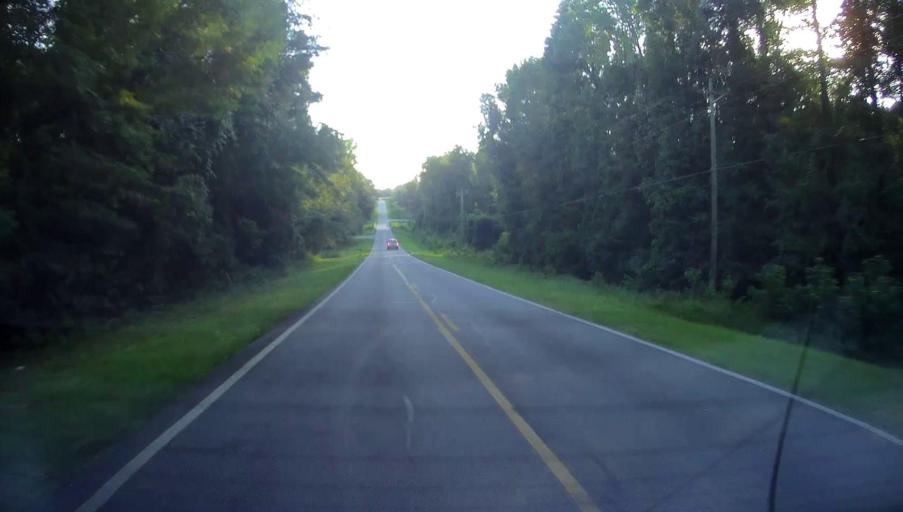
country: US
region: Georgia
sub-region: Peach County
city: Byron
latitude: 32.6252
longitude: -83.8208
